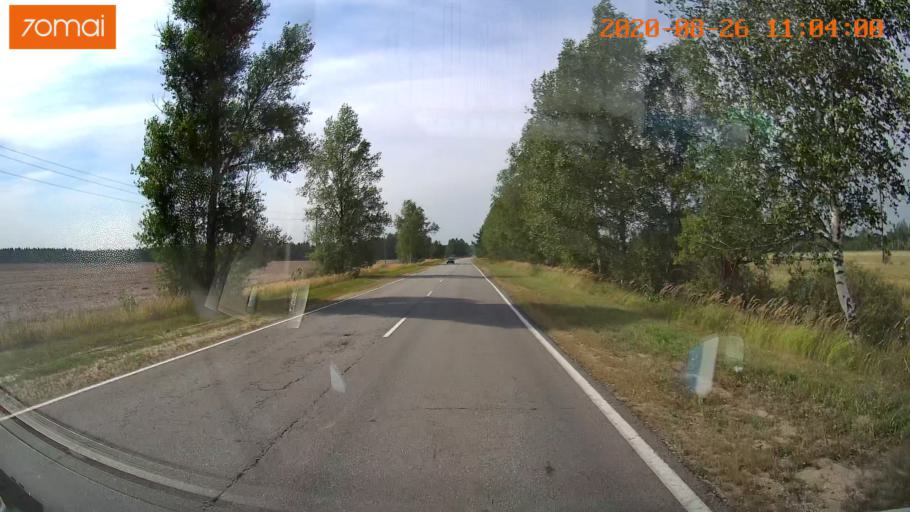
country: RU
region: Rjazan
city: Izhevskoye
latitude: 54.5348
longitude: 41.2029
